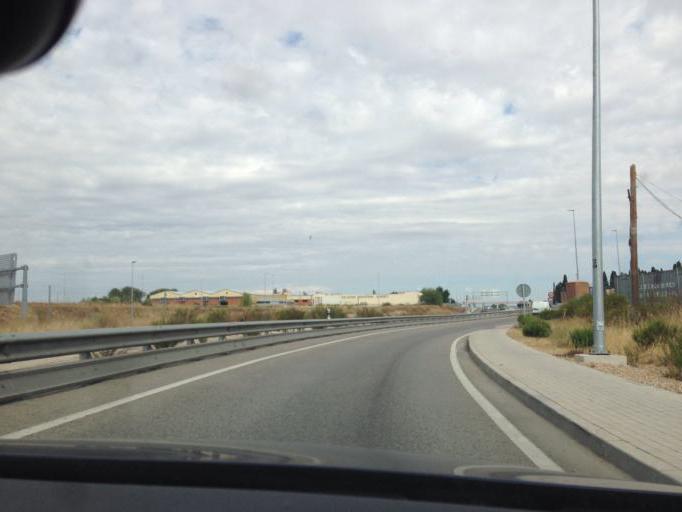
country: ES
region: Madrid
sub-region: Provincia de Madrid
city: Alcala de Henares
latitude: 40.5009
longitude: -3.3968
